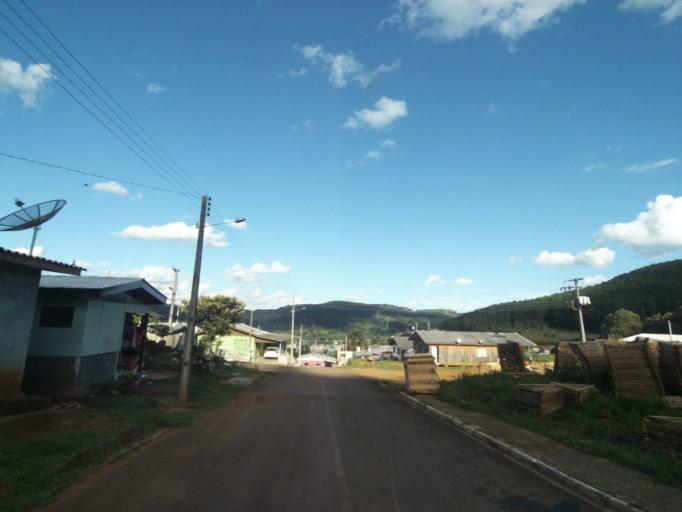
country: BR
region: Parana
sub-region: Uniao Da Vitoria
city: Uniao da Vitoria
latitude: -26.1675
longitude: -51.5385
